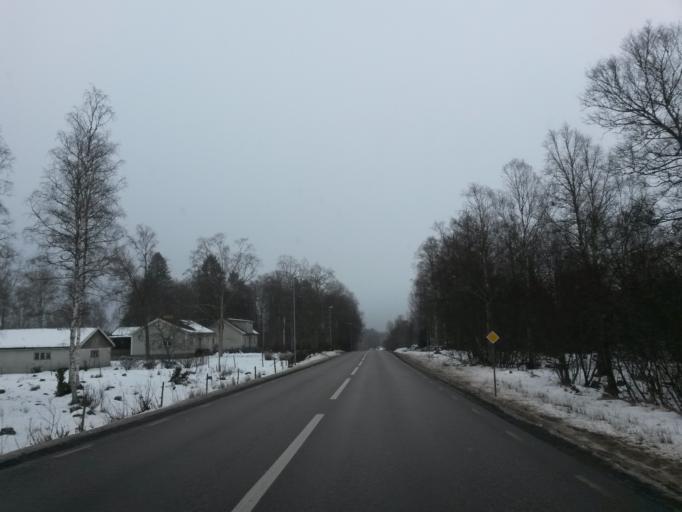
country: SE
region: Vaestra Goetaland
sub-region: Ulricehamns Kommun
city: Ulricehamn
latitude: 57.9028
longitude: 13.3387
